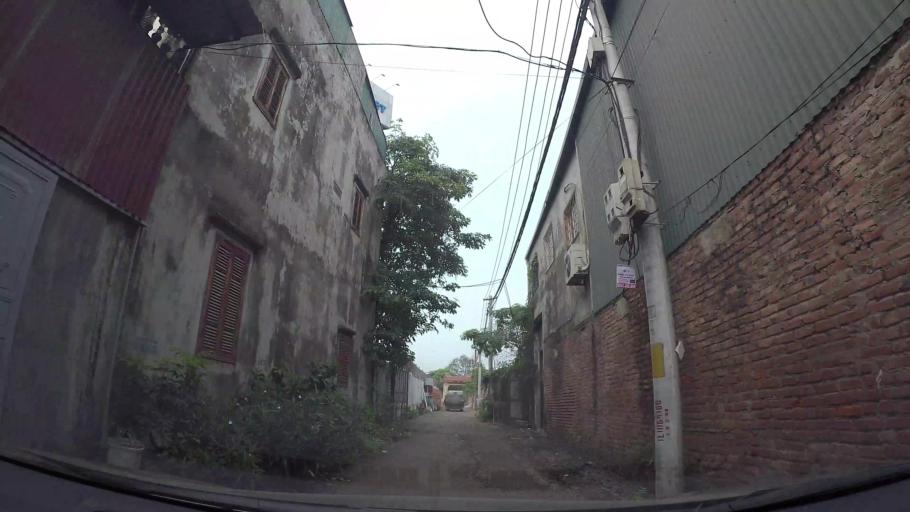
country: VN
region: Ha Noi
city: Van Dien
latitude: 20.9709
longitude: 105.8666
